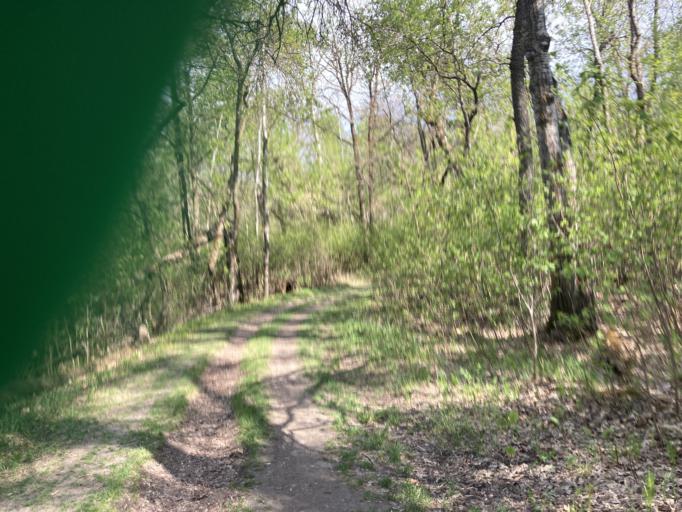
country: CA
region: Manitoba
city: Brandon
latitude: 49.7206
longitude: -99.9065
